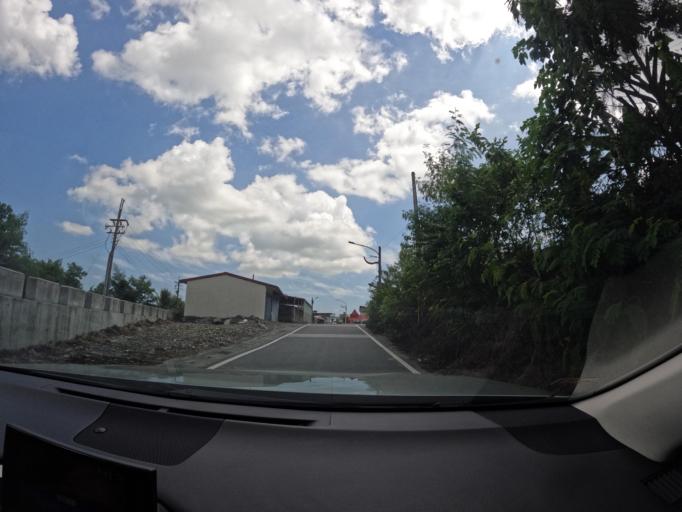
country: TW
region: Taiwan
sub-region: Hualien
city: Hualian
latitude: 23.7174
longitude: 121.4082
